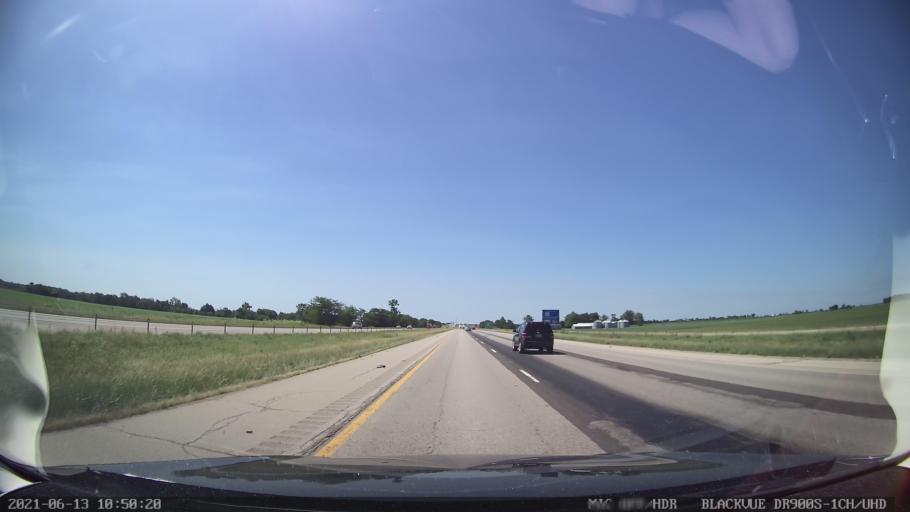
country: US
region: Illinois
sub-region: Sangamon County
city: Divernon
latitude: 39.6066
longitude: -89.6436
